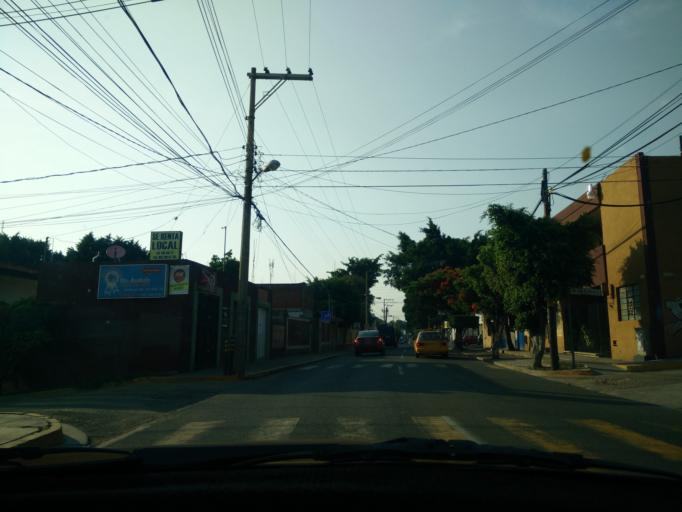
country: MX
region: Oaxaca
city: Oaxaca de Juarez
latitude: 17.0758
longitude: -96.7396
